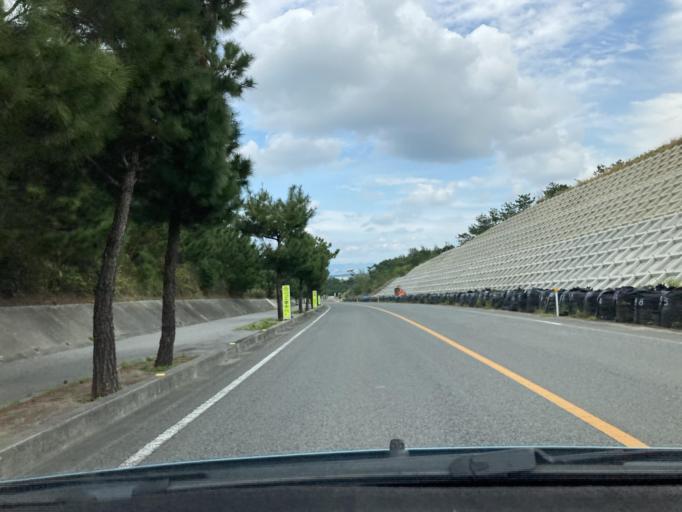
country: JP
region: Okinawa
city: Ishikawa
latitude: 26.4609
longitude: 127.8257
